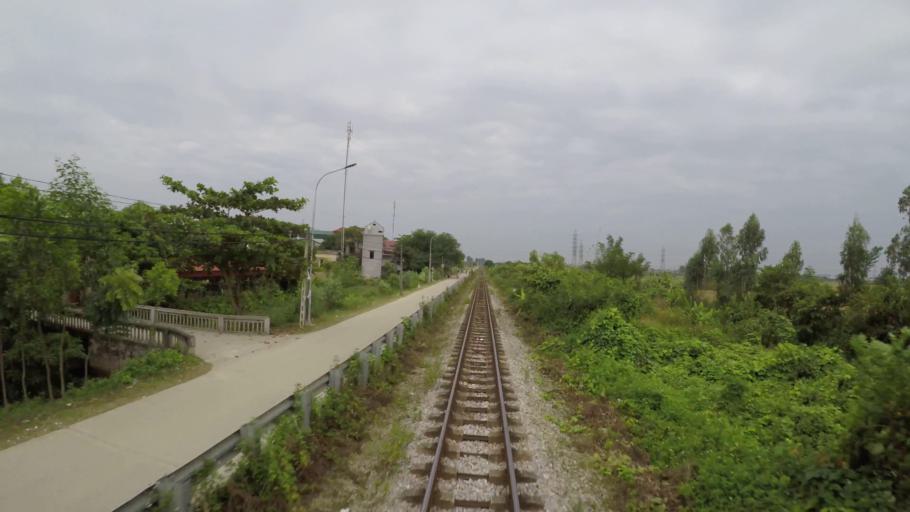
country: VN
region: Hai Duong
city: Lai Cach
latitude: 20.9505
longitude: 106.2420
